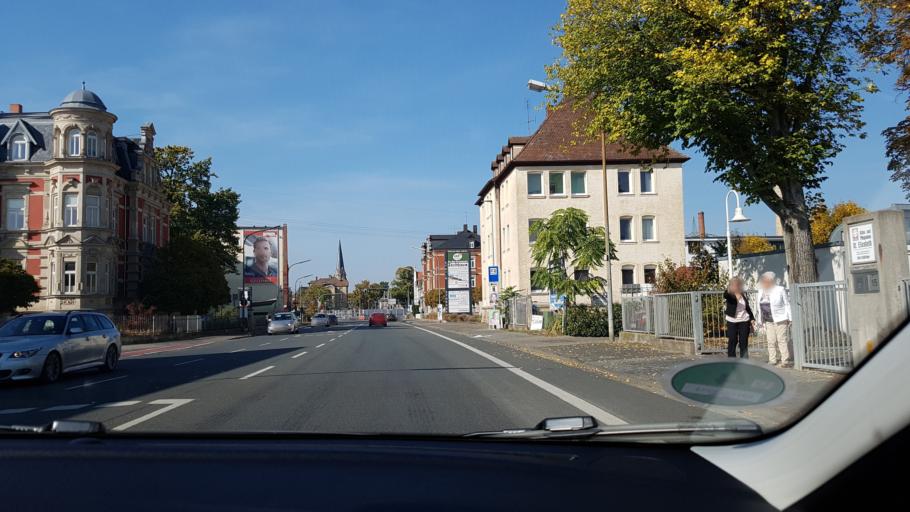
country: DE
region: Bavaria
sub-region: Upper Franconia
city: Forchheim
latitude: 49.7172
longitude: 11.0731
